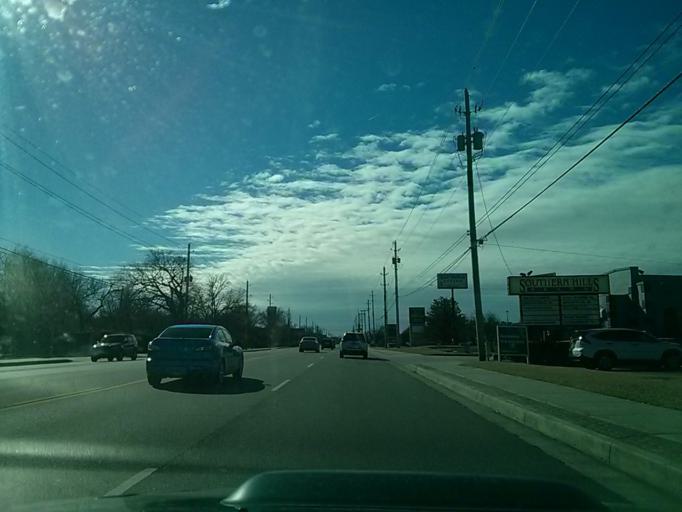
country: US
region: Oklahoma
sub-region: Tulsa County
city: Jenks
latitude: 36.0717
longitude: -95.9582
